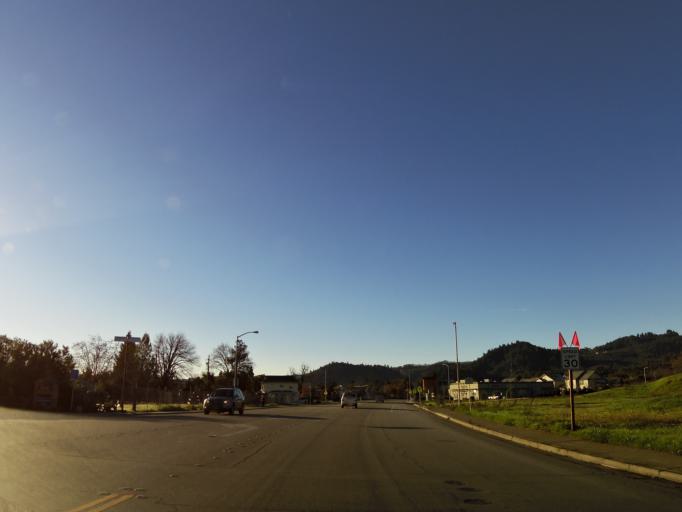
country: US
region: California
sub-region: Sonoma County
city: Cloverdale
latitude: 38.8019
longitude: -123.0161
